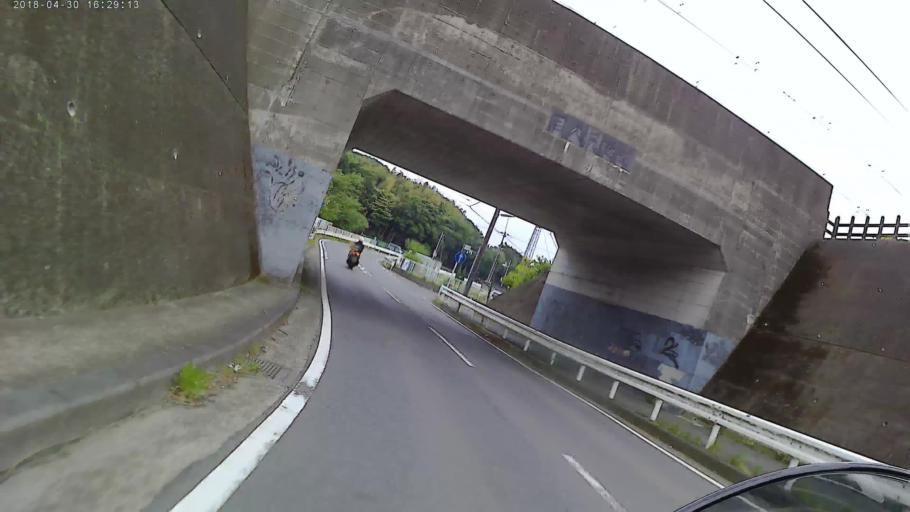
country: JP
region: Kanagawa
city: Zama
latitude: 35.4593
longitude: 139.4054
